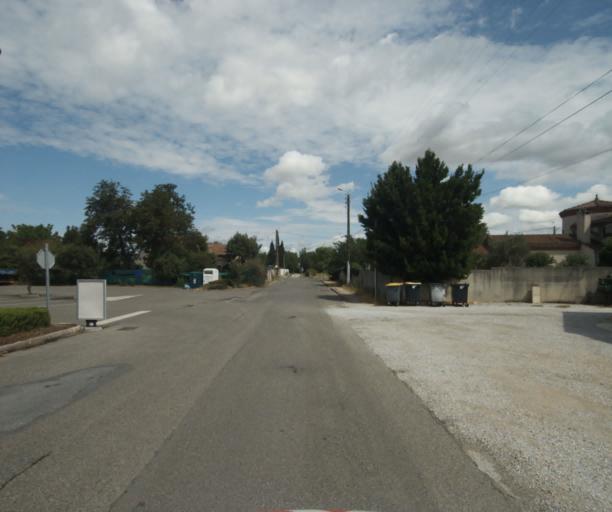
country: FR
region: Midi-Pyrenees
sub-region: Departement de la Haute-Garonne
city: Revel
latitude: 43.4636
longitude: 2.0059
